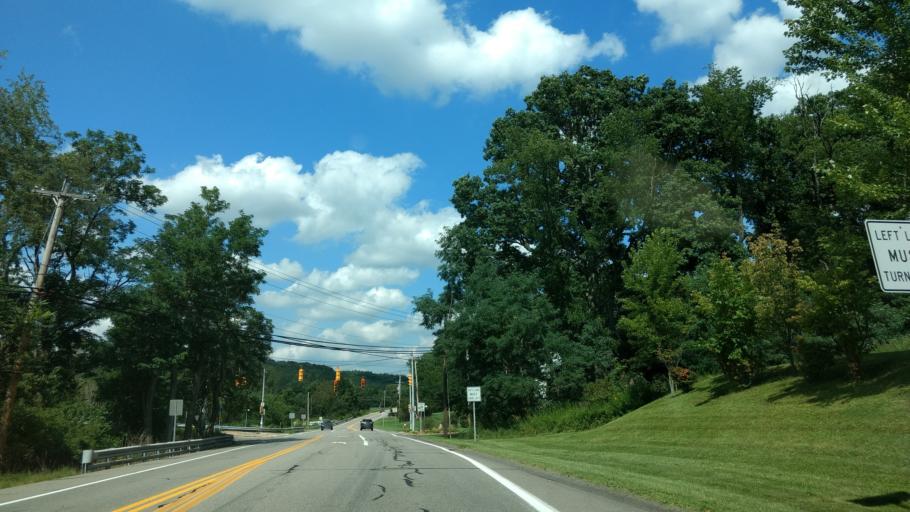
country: US
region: Pennsylvania
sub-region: Allegheny County
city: West View
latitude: 40.5862
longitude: -80.0228
